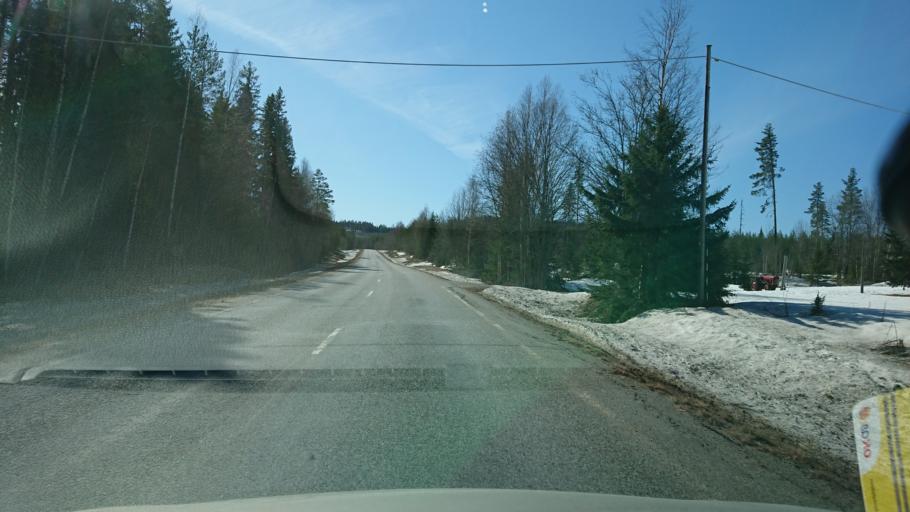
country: SE
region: Vaesterbotten
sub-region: Dorotea Kommun
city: Dorotea
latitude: 64.0034
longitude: 16.3049
